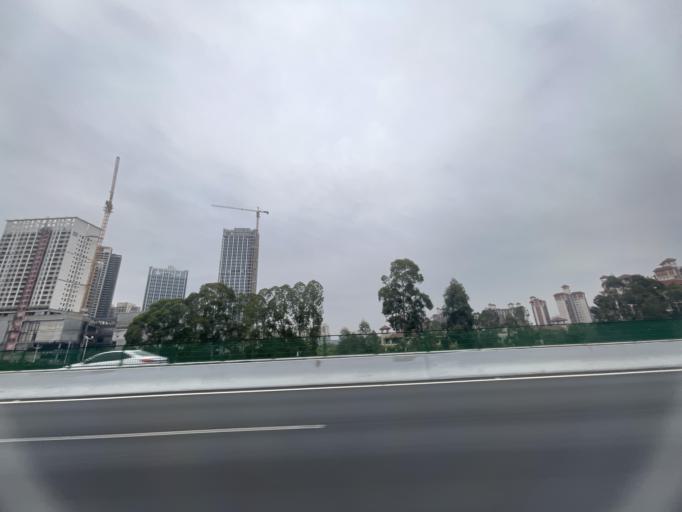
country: CN
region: Guangdong
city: Huangge
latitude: 22.7897
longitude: 113.5153
